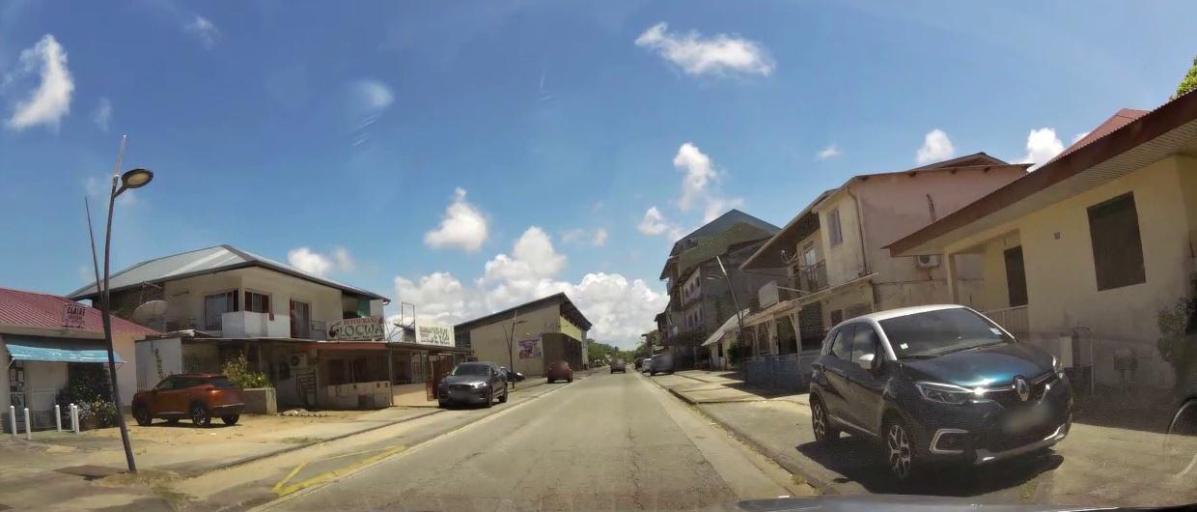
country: GF
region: Guyane
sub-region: Guyane
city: Kourou
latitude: 5.1562
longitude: -52.6432
